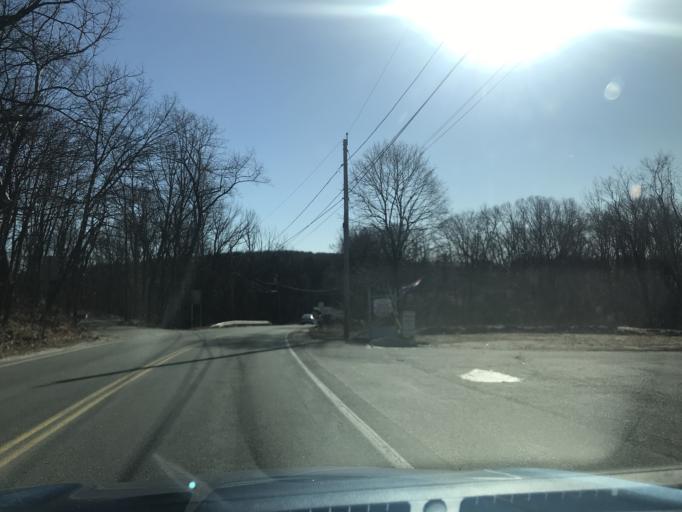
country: US
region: Massachusetts
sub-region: Essex County
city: North Andover
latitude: 42.7124
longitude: -71.0818
